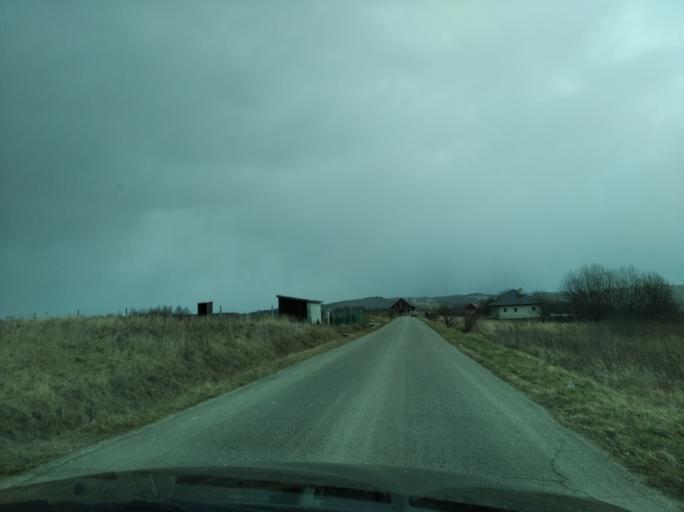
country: PL
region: Subcarpathian Voivodeship
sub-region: Powiat rzeszowski
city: Hyzne
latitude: 49.9032
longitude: 22.1818
